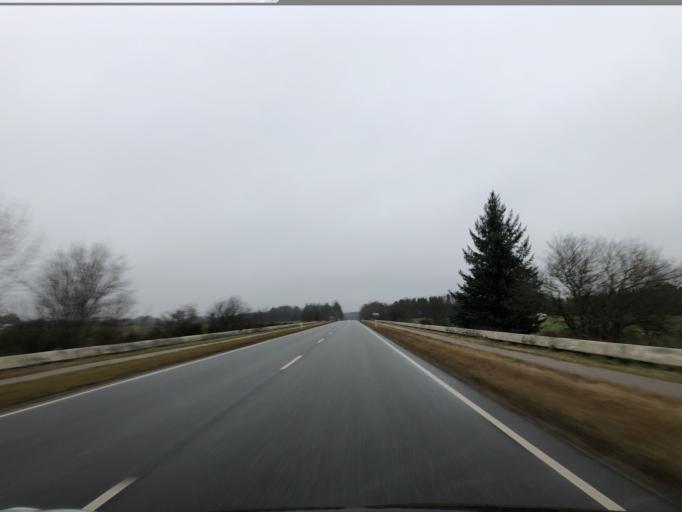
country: DK
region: Central Jutland
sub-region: Herning Kommune
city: Lind
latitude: 56.0727
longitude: 8.9878
